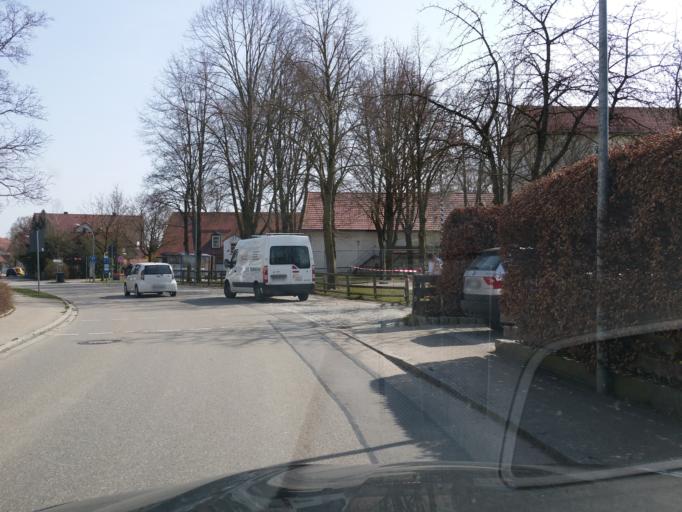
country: DE
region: Bavaria
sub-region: Upper Bavaria
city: Langenpreising
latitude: 48.4244
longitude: 11.9710
